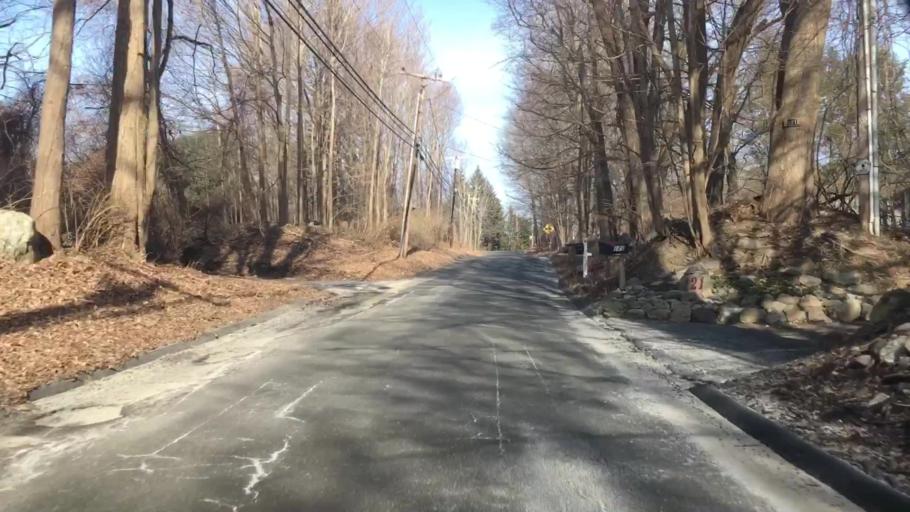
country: US
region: Connecticut
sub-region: Fairfield County
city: Danbury
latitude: 41.3651
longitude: -73.5022
